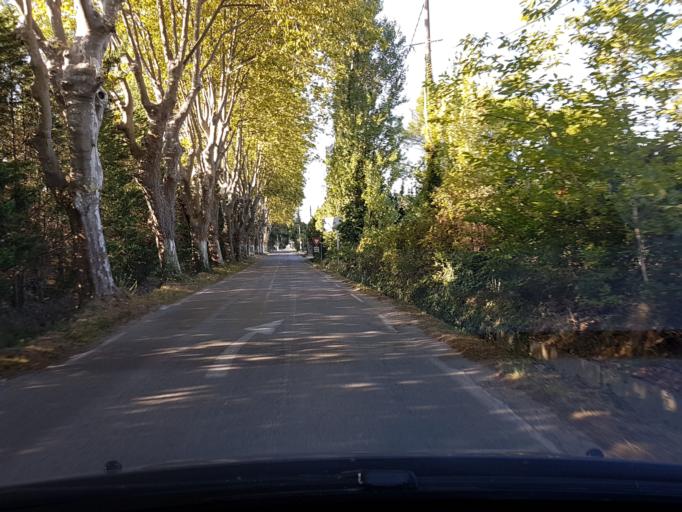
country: FR
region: Provence-Alpes-Cote d'Azur
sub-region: Departement des Bouches-du-Rhone
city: Eygalieres
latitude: 43.7832
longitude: 4.9270
